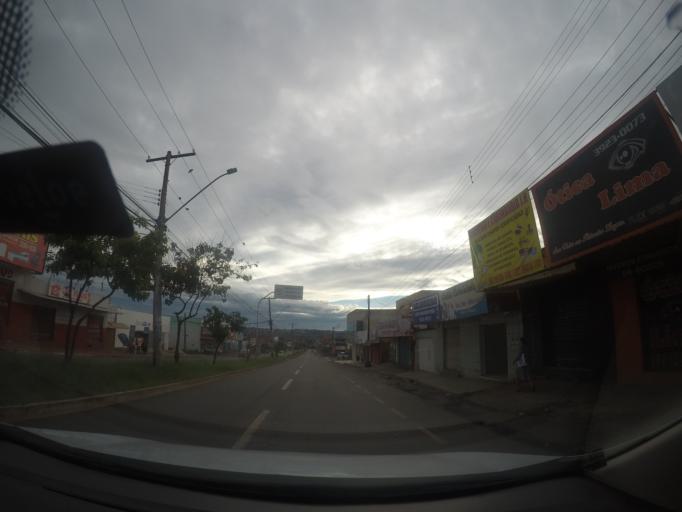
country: BR
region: Goias
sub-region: Goiania
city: Goiania
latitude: -16.6152
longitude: -49.3467
